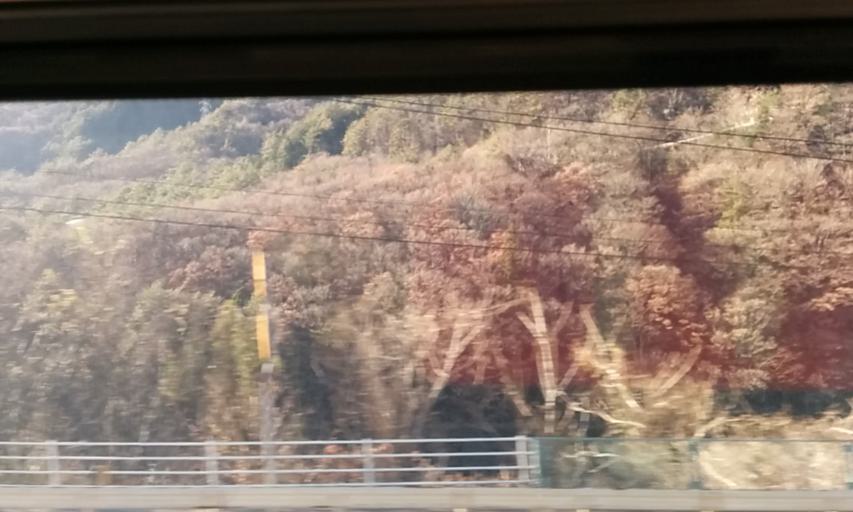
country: JP
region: Nagano
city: Iida
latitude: 35.7192
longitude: 137.7100
